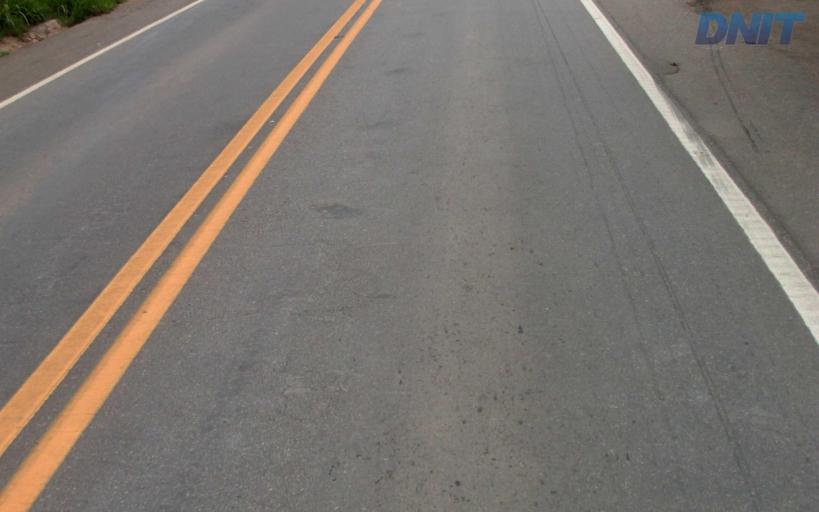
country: BR
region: Minas Gerais
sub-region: Governador Valadares
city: Governador Valadares
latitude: -18.9528
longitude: -42.0726
